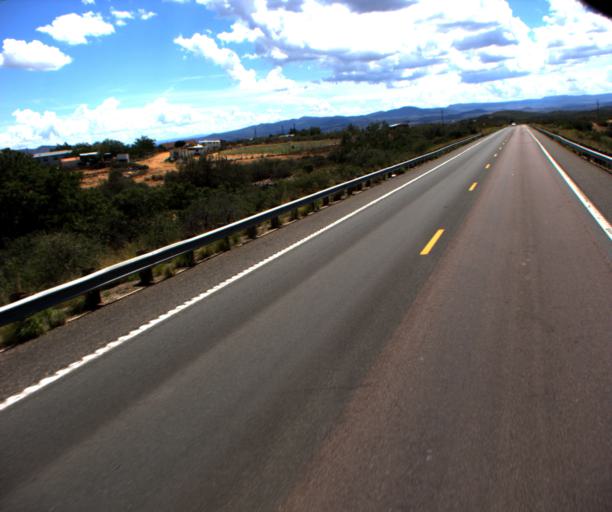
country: US
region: Arizona
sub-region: Yavapai County
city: Dewey-Humboldt
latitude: 34.5400
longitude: -112.1491
